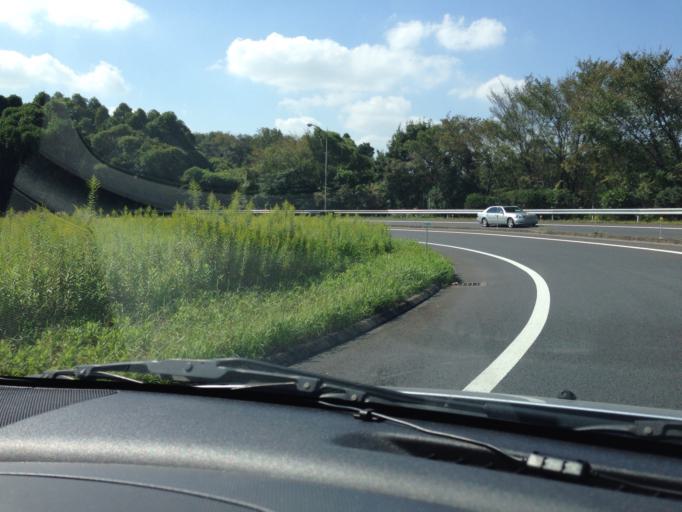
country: JP
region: Ibaraki
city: Naka
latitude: 36.0609
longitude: 140.1584
